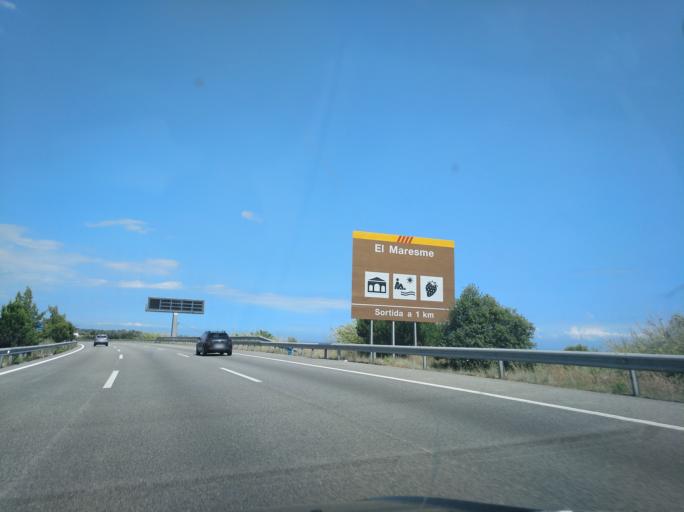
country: ES
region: Catalonia
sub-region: Provincia de Barcelona
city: Arenys de Mar
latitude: 41.5907
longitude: 2.5559
